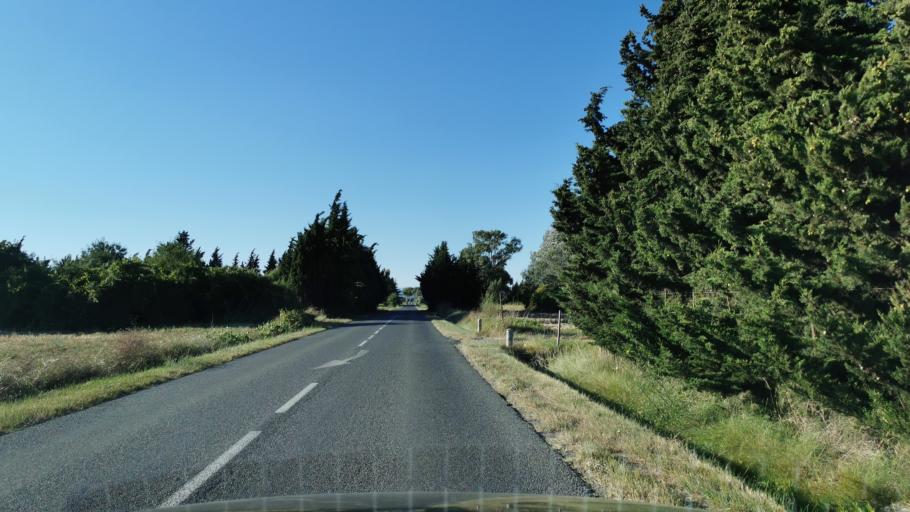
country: FR
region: Languedoc-Roussillon
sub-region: Departement de l'Aude
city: Ouveillan
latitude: 43.2555
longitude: 2.9964
